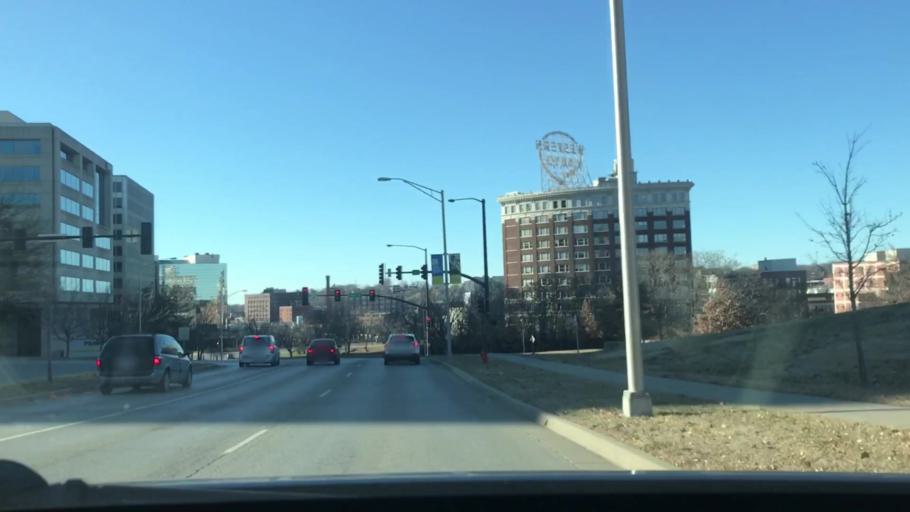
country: US
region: Missouri
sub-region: Jackson County
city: Kansas City
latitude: 39.0865
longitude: -94.5782
